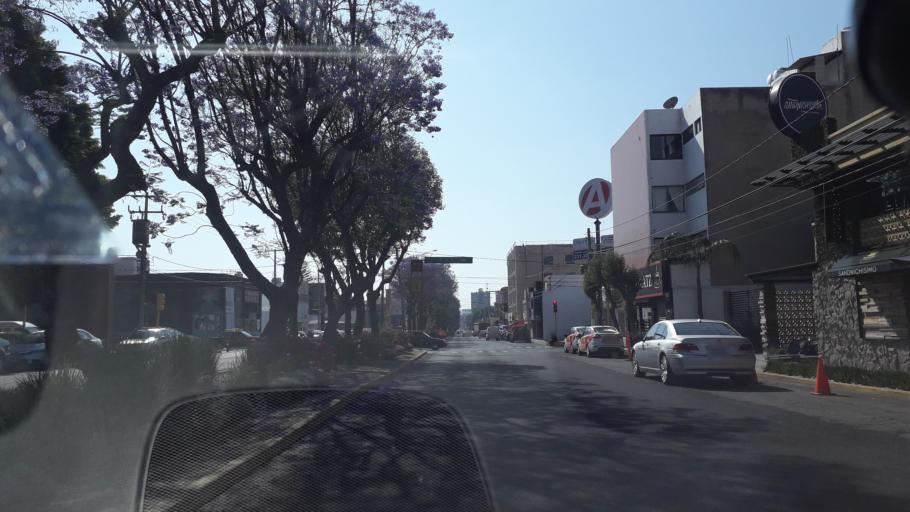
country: MX
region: Puebla
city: Puebla
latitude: 19.0304
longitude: -98.2134
